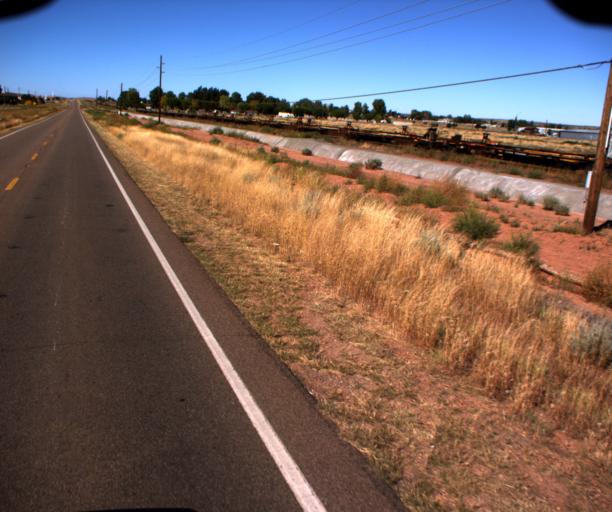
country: US
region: Arizona
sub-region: Navajo County
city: Snowflake
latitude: 34.5131
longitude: -110.1099
